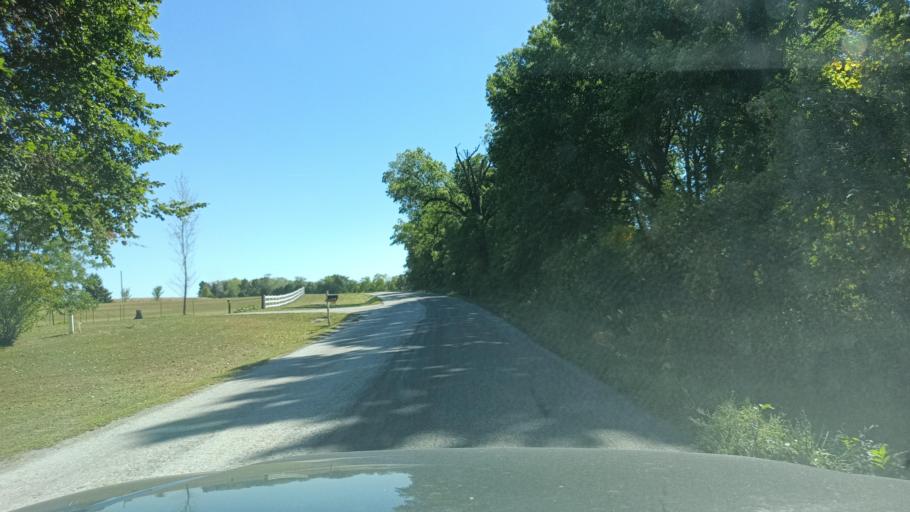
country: US
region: Missouri
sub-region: Macon County
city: La Plata
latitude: 40.0178
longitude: -92.6001
